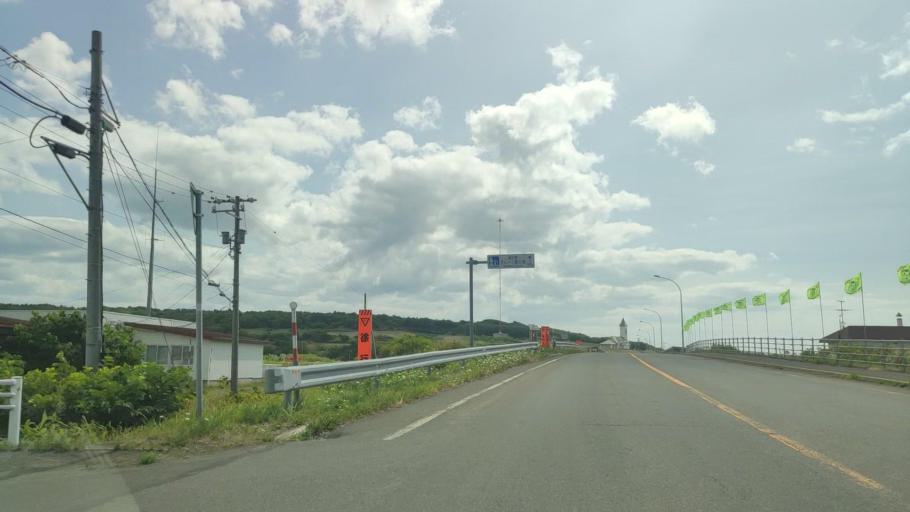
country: JP
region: Hokkaido
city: Makubetsu
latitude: 44.7192
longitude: 141.7933
